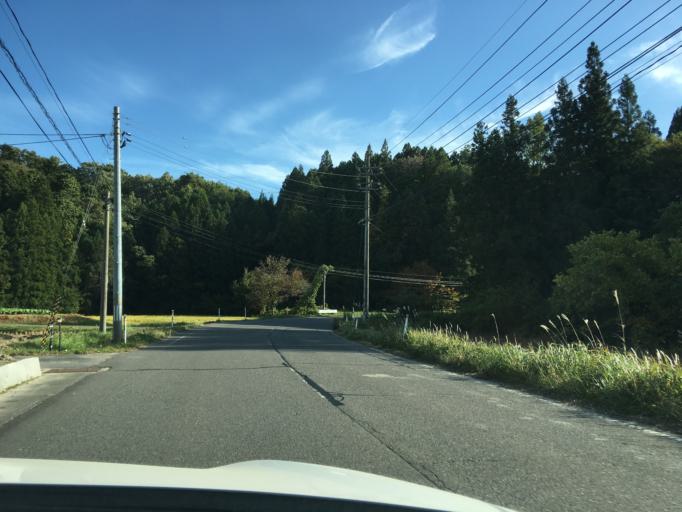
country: JP
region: Fukushima
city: Funehikimachi-funehiki
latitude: 37.3285
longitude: 140.5920
